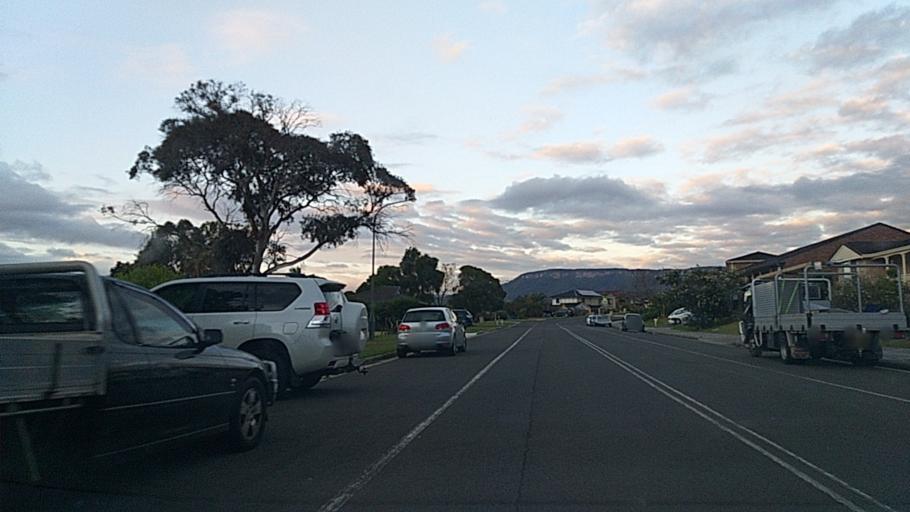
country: AU
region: New South Wales
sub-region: Wollongong
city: Dapto
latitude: -34.4935
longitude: 150.7807
